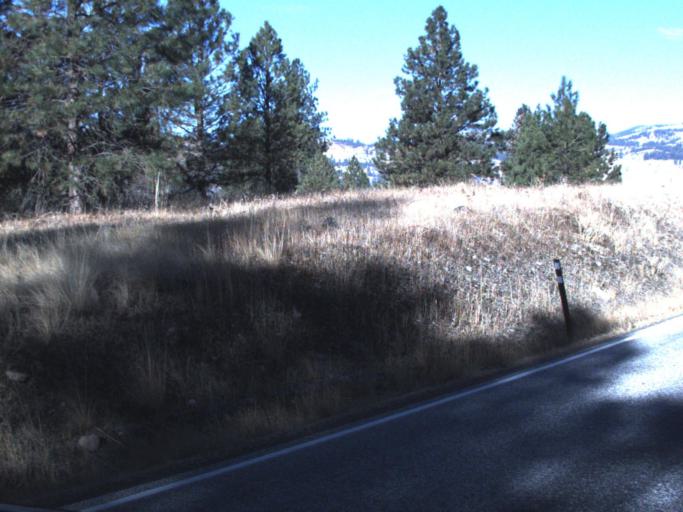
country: US
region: Washington
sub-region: Ferry County
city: Republic
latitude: 48.7305
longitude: -118.6541
